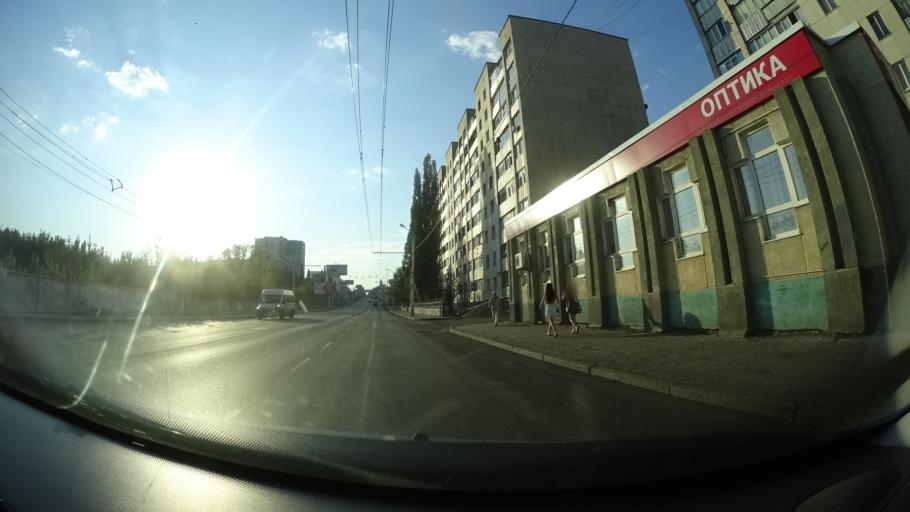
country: RU
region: Bashkortostan
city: Sterlitamak
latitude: 53.6214
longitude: 55.9565
